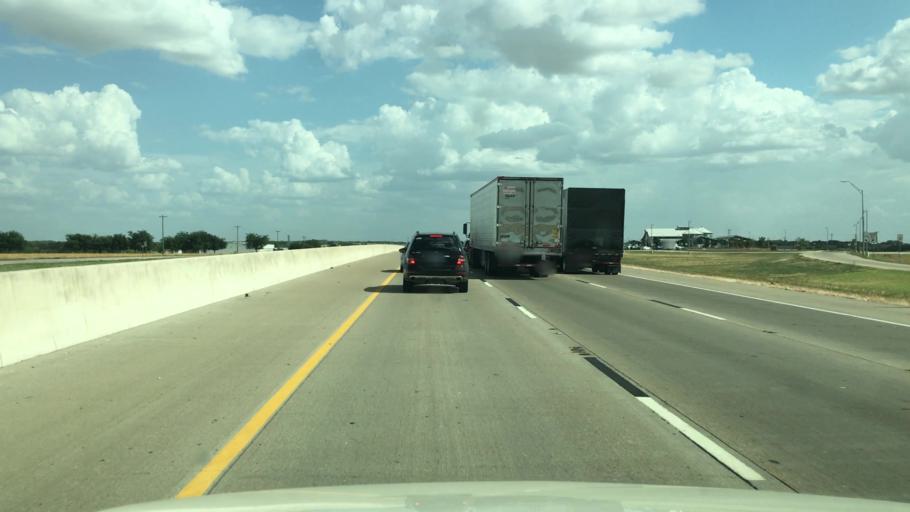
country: US
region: Texas
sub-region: Hill County
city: Hillsboro
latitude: 31.9301
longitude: -97.1036
